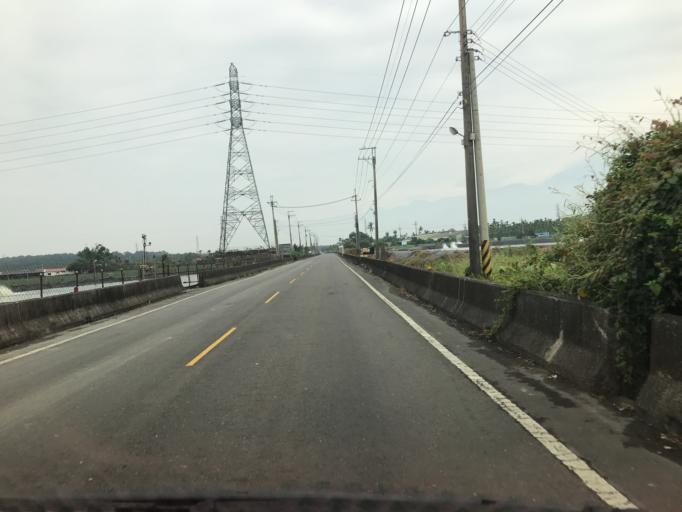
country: TW
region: Taiwan
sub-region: Pingtung
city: Pingtung
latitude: 22.5362
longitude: 120.5590
